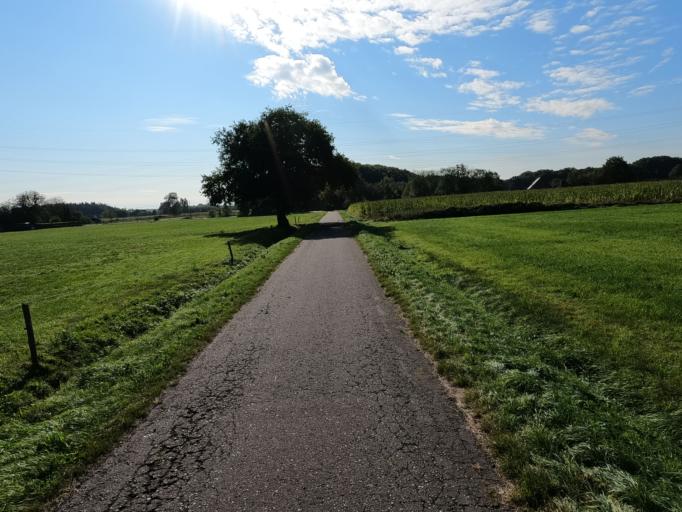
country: BE
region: Flanders
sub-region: Provincie Antwerpen
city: Zandhoven
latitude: 51.2256
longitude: 4.6582
